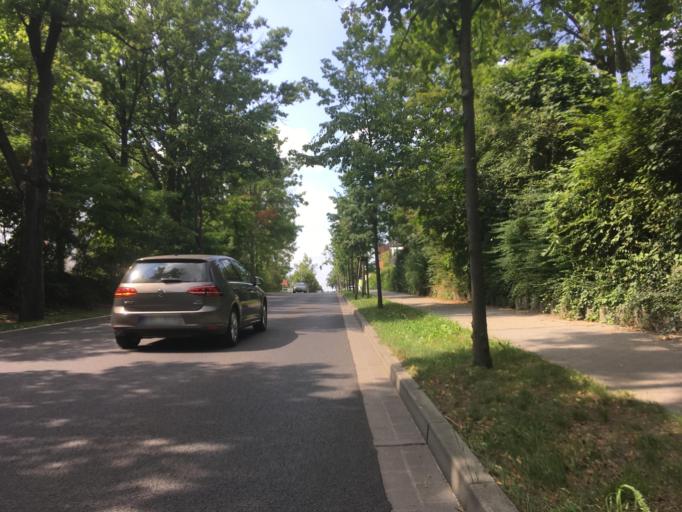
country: DE
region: Brandenburg
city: Wildau
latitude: 52.3170
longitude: 13.6255
